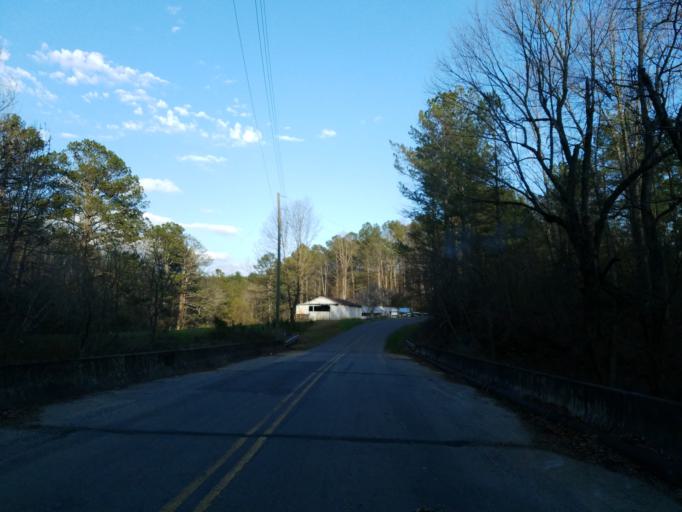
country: US
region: Georgia
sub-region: Pickens County
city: Jasper
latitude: 34.5084
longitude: -84.6040
